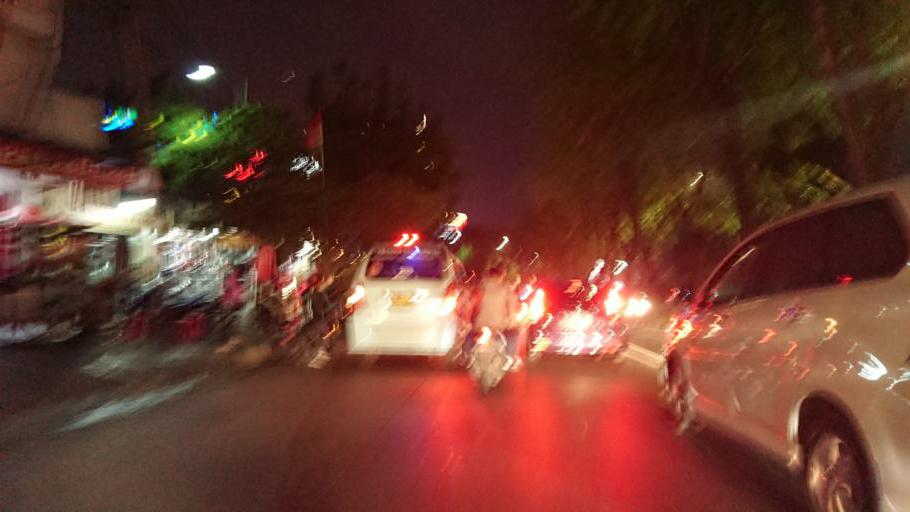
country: ID
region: Jakarta Raya
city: Jakarta
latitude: -6.2424
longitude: 106.7827
